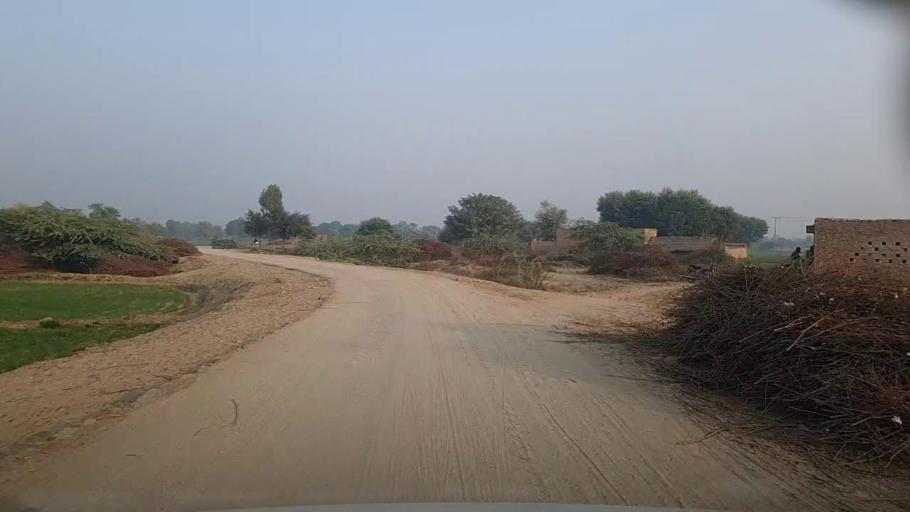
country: PK
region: Sindh
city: Bozdar
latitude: 27.0838
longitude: 68.5633
